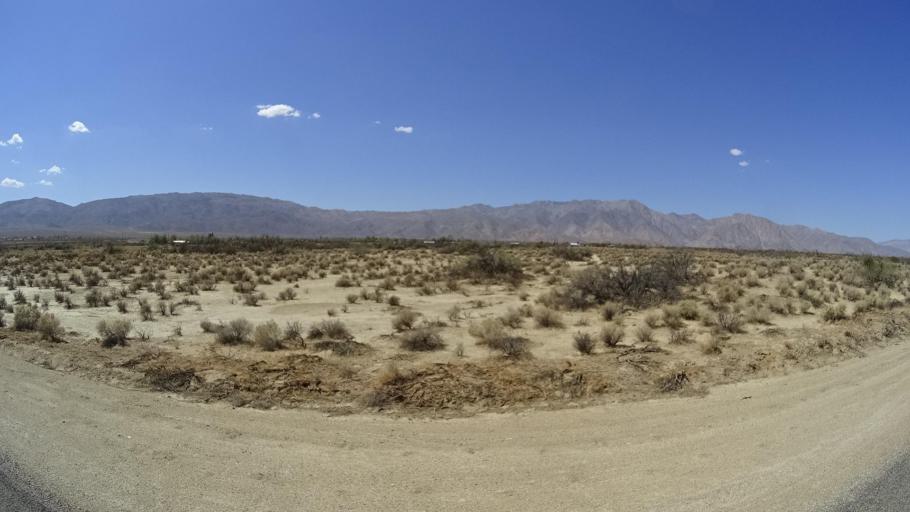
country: US
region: California
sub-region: San Diego County
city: Borrego Springs
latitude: 33.2259
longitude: -116.3303
